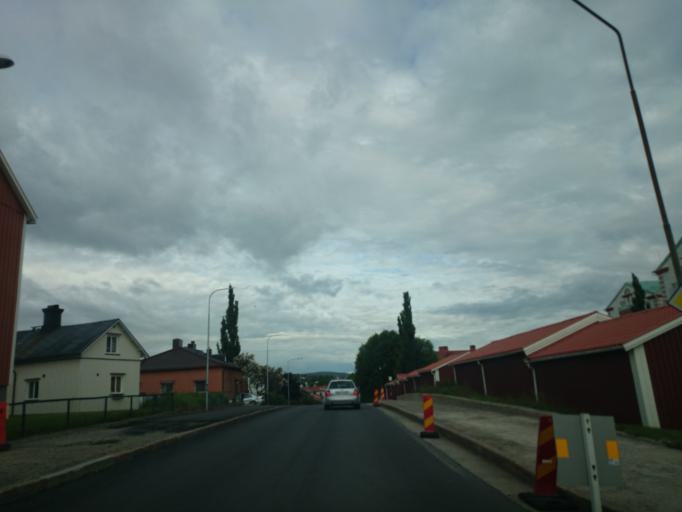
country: SE
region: Vaesternorrland
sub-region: Sundsvalls Kommun
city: Sundsvall
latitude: 62.3807
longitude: 17.3296
